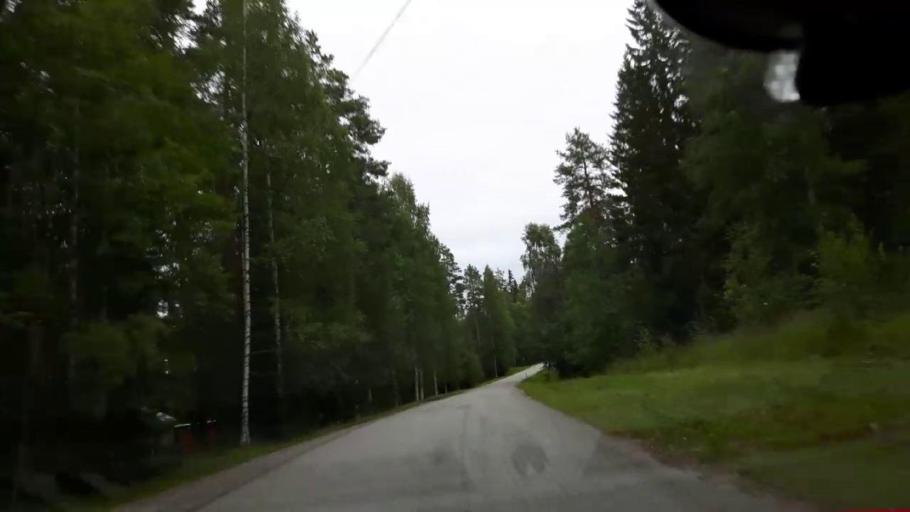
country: SE
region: Vaesternorrland
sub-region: Ange Kommun
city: Fransta
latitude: 62.7709
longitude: 16.0108
